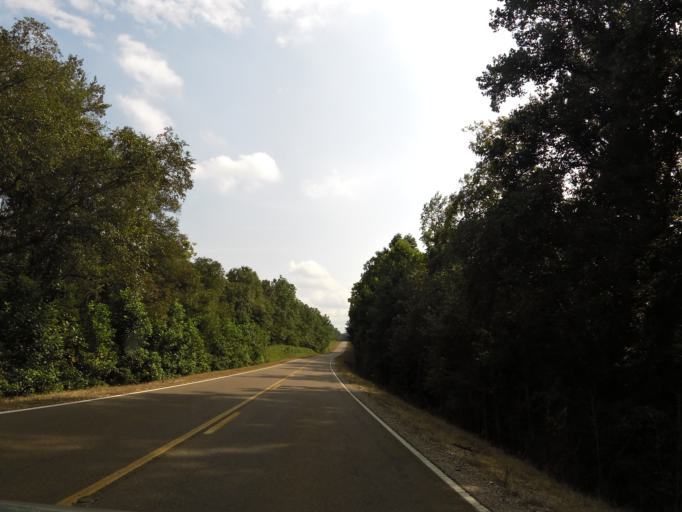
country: US
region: Tennessee
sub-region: Hardin County
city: Crump
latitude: 35.1310
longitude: -88.3611
